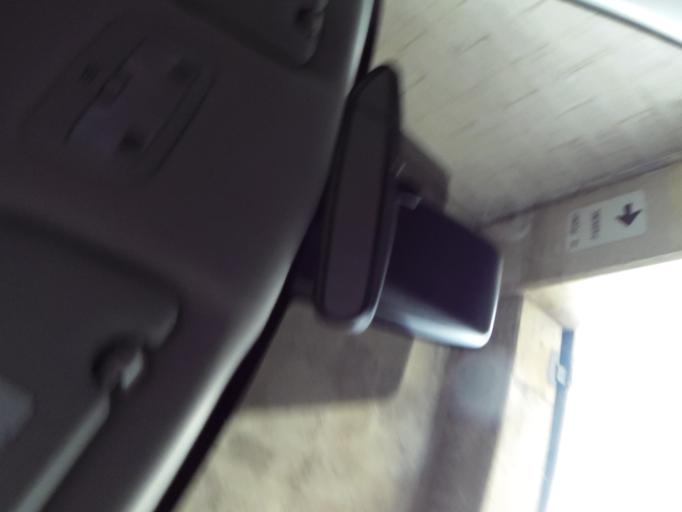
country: US
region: Minnesota
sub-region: Hennepin County
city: Minnetonka Mills
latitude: 44.9142
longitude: -93.4229
